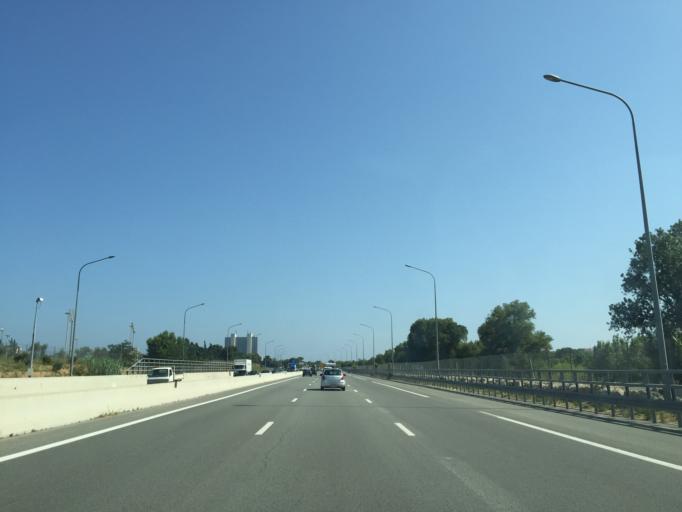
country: FR
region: Provence-Alpes-Cote d'Azur
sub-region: Departement des Alpes-Maritimes
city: Saint-Laurent-du-Var
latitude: 43.6822
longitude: 7.1925
